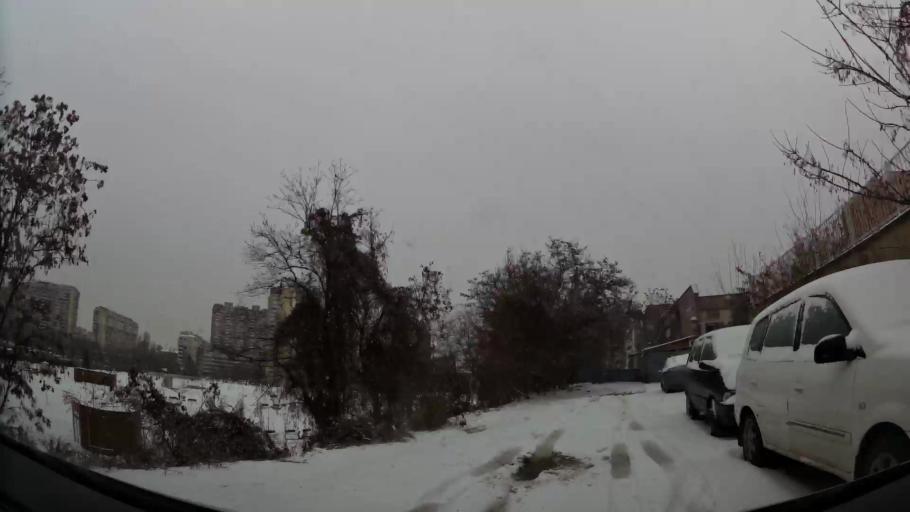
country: BG
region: Sofia-Capital
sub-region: Stolichna Obshtina
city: Sofia
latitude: 42.6937
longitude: 23.3073
